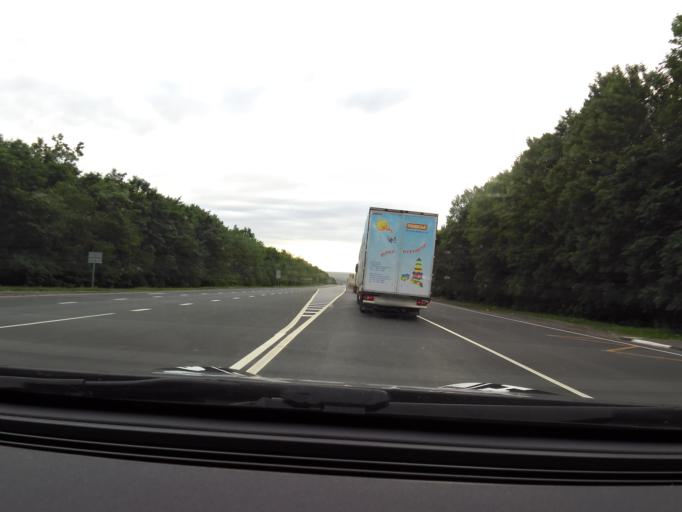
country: RU
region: Chuvashia
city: Tsivil'sk
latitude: 55.8393
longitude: 47.5407
